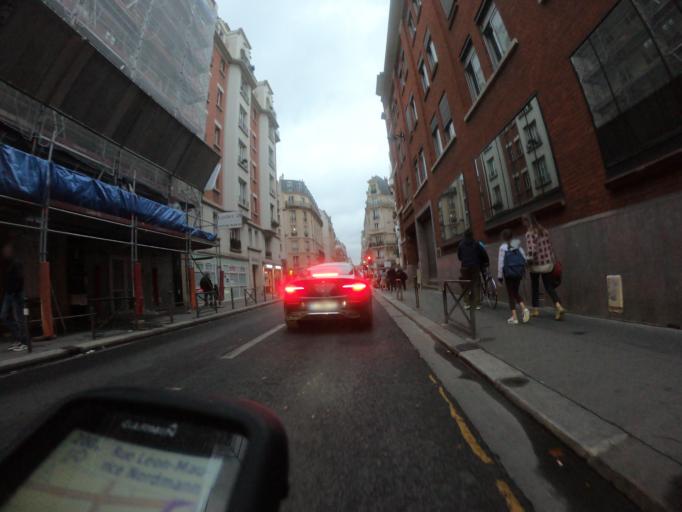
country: FR
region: Ile-de-France
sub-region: Paris
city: Paris
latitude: 48.8336
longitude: 2.3448
